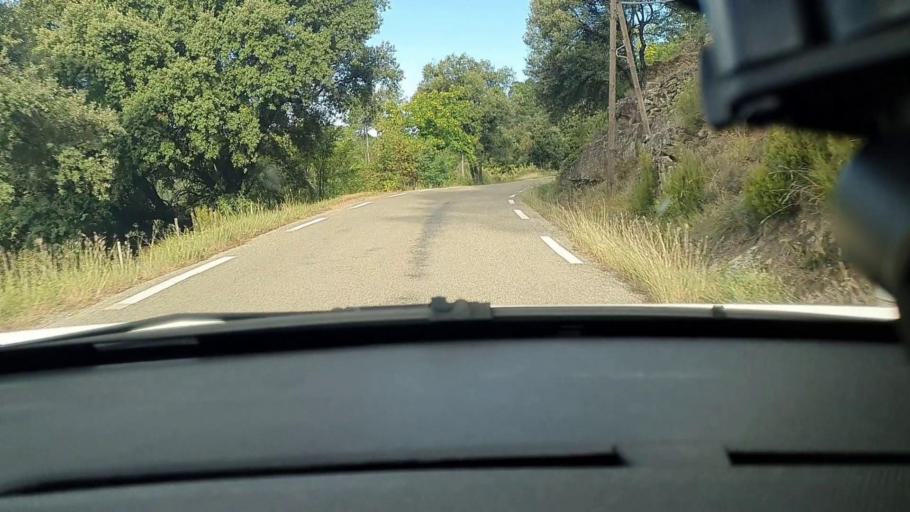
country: FR
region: Languedoc-Roussillon
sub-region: Departement du Gard
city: Besseges
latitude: 44.3084
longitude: 4.0801
